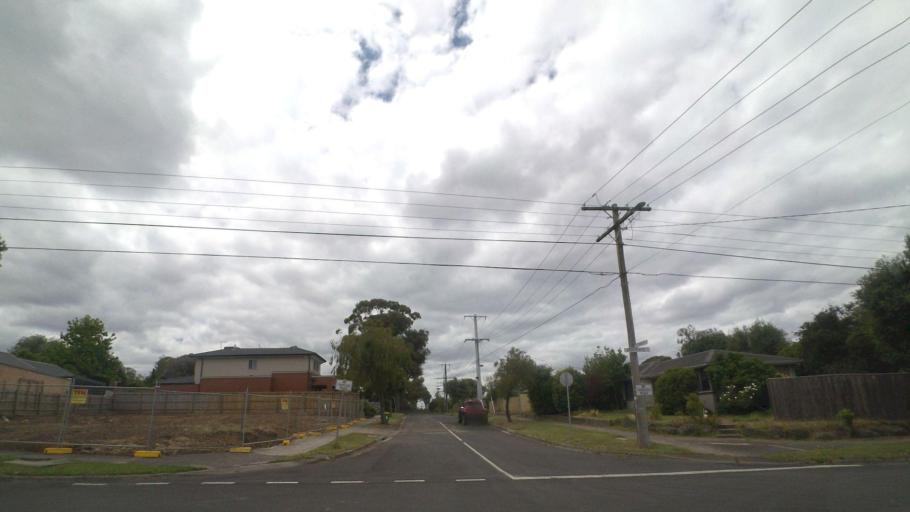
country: AU
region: Victoria
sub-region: Knox
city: Bayswater
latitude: -37.8601
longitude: 145.2467
